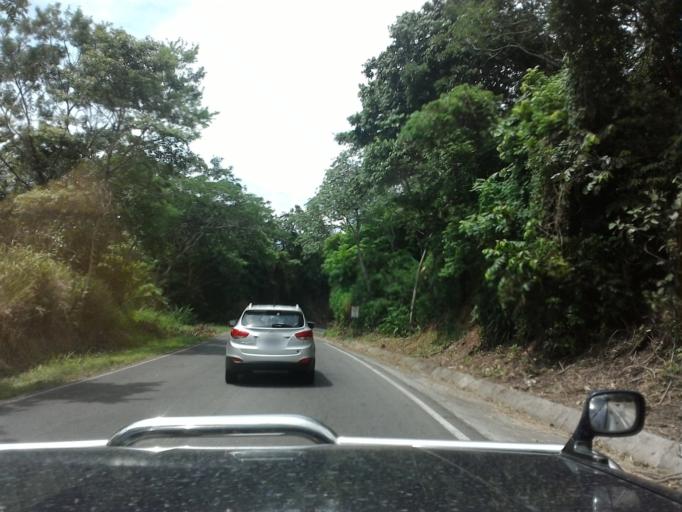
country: CR
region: Puntarenas
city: Esparza
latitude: 10.0271
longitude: -84.5775
